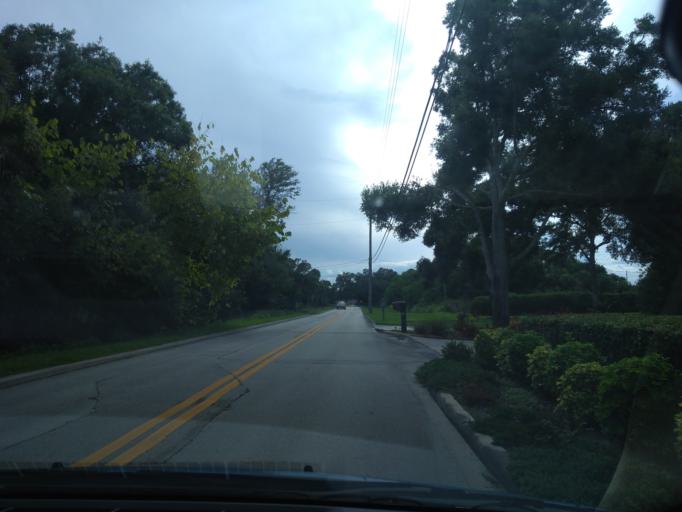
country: US
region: Florida
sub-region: Indian River County
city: Vero Beach South
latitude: 27.6316
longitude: -80.4418
